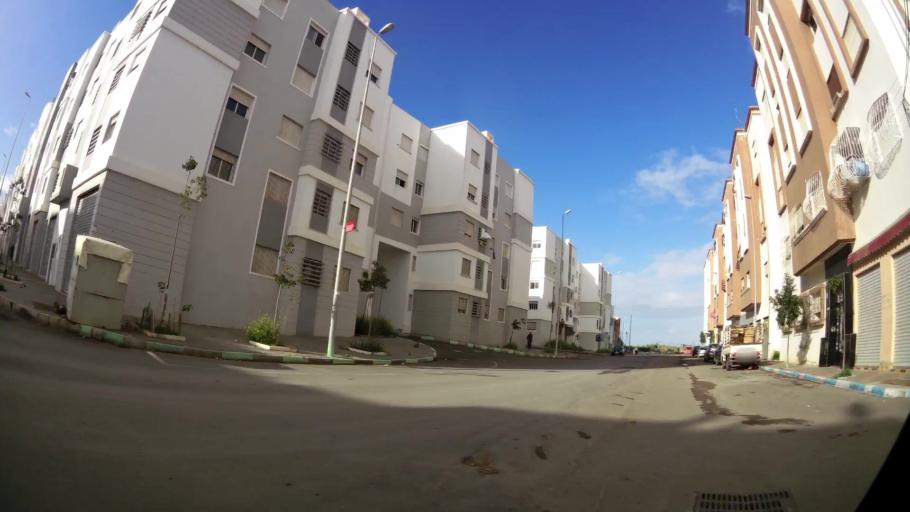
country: MA
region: Grand Casablanca
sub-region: Casablanca
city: Casablanca
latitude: 33.5505
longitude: -7.7016
